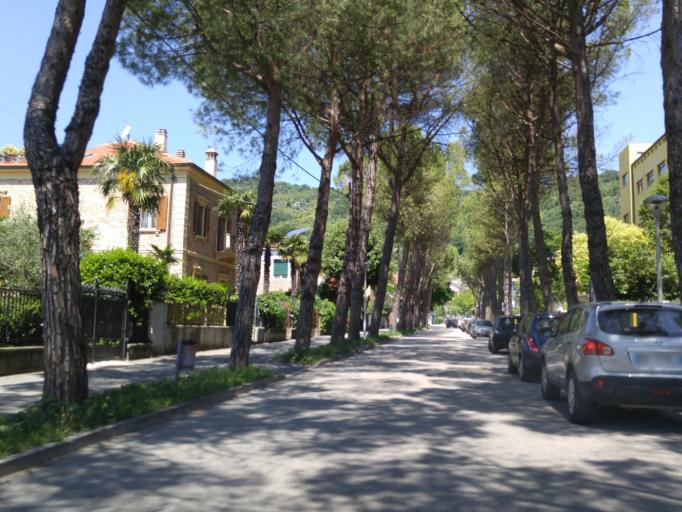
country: IT
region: The Marches
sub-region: Provincia di Pesaro e Urbino
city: Fossombrone
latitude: 43.6905
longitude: 12.8163
